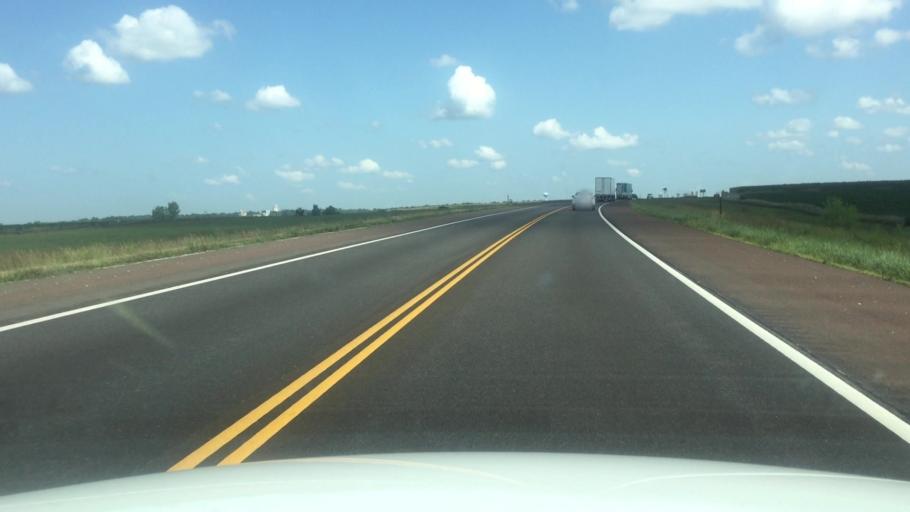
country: US
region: Kansas
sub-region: Nemaha County
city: Sabetha
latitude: 39.8760
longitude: -95.7809
